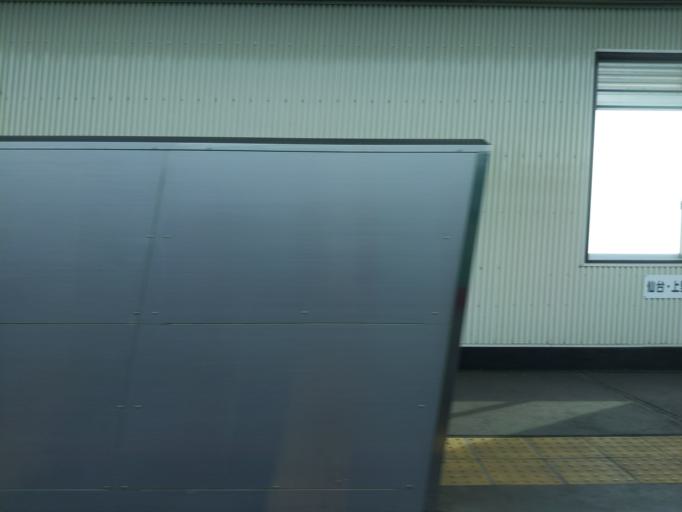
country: JP
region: Iwate
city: Ichinoseki
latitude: 38.7481
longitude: 141.0713
